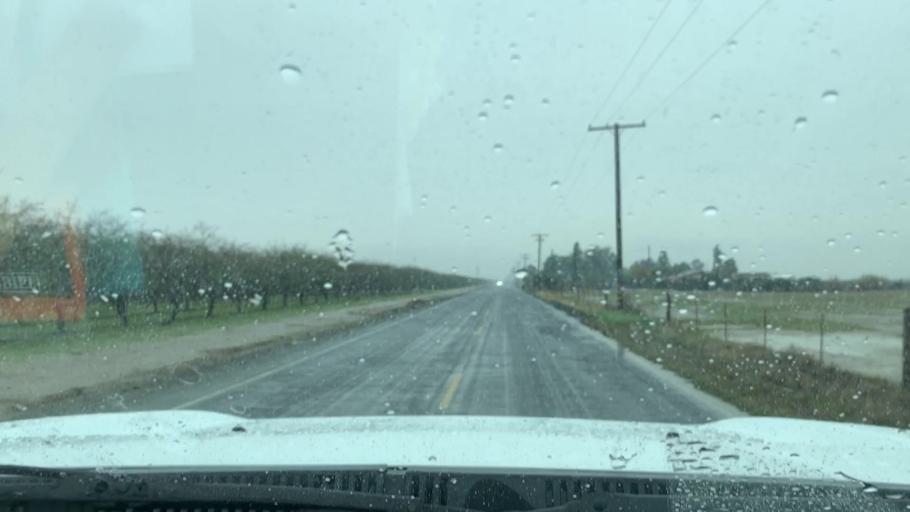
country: US
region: California
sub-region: Tulare County
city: Earlimart
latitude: 35.8919
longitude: -119.3250
